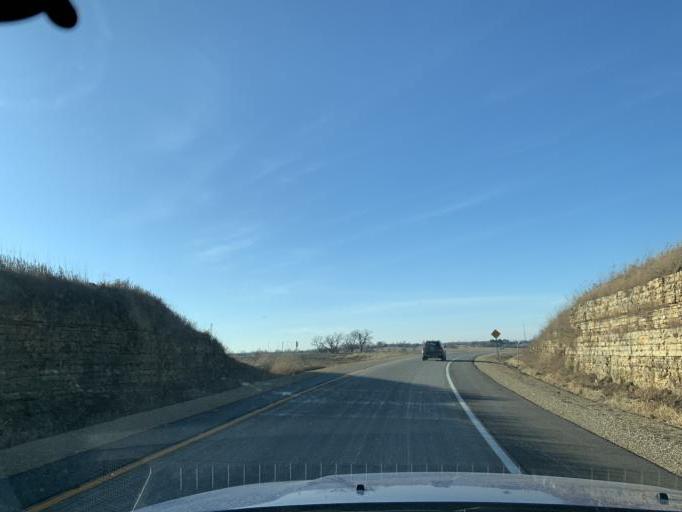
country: US
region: Wisconsin
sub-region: Iowa County
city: Dodgeville
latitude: 42.9653
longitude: -90.1038
